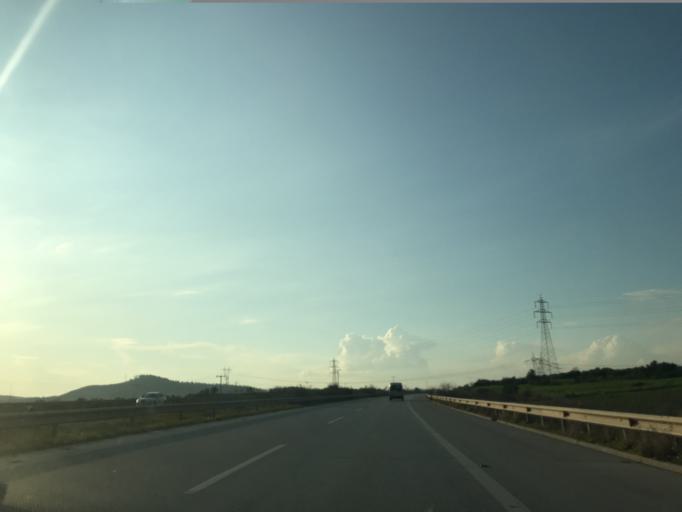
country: TR
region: Osmaniye
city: Toprakkale
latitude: 36.9680
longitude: 36.0355
